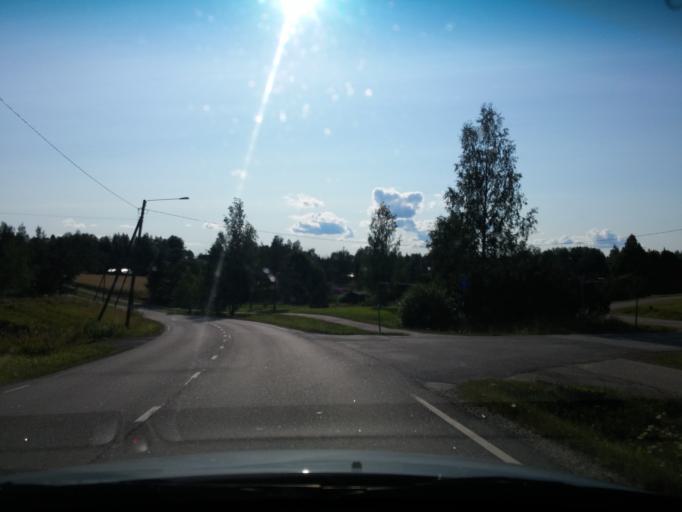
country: FI
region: Uusimaa
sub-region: Porvoo
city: Askola
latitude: 60.4955
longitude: 25.5461
